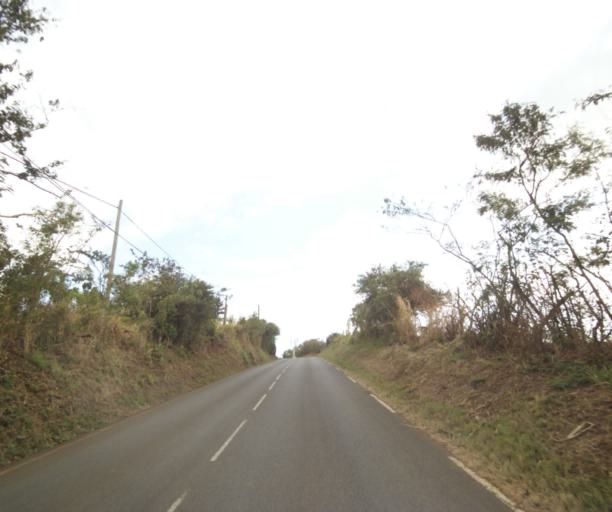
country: RE
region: Reunion
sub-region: Reunion
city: Trois-Bassins
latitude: -21.0672
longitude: 55.2783
